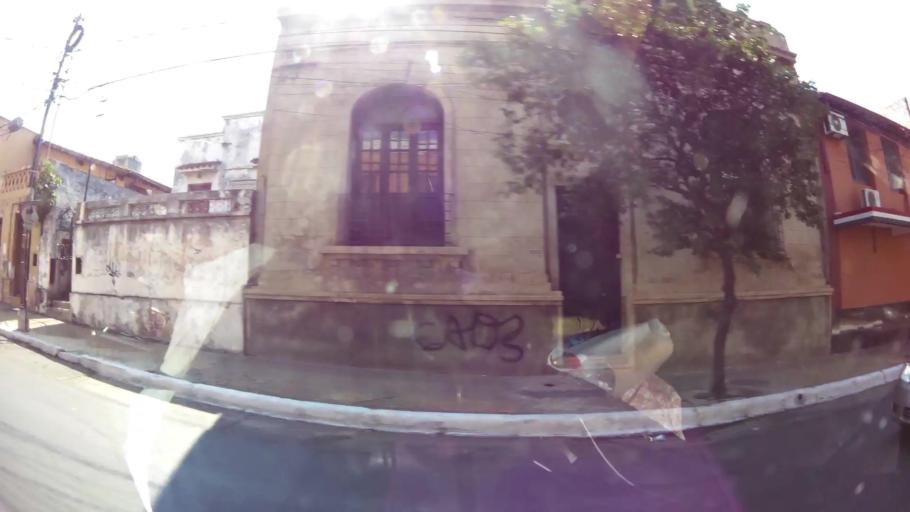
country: PY
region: Asuncion
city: Asuncion
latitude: -25.2909
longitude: -57.6288
